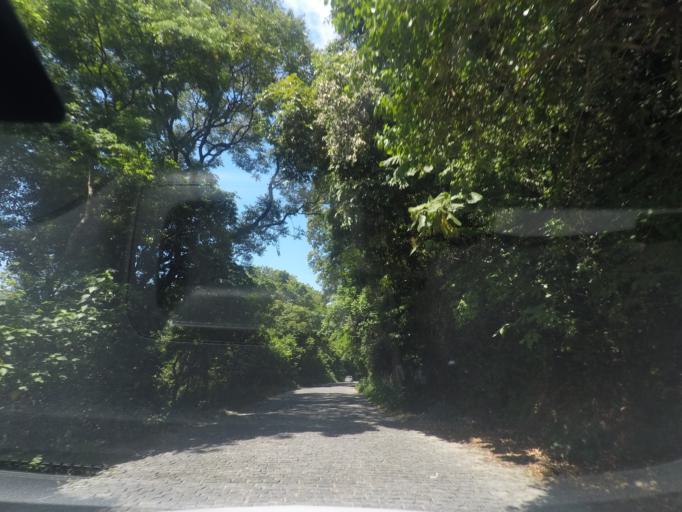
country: BR
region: Rio de Janeiro
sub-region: Petropolis
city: Petropolis
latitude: -22.5494
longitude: -43.1821
